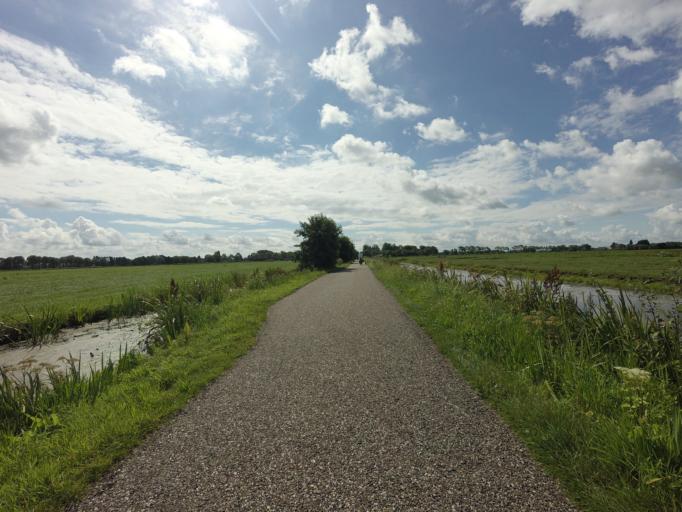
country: NL
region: South Holland
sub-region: Molenwaard
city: Liesveld
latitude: 51.9415
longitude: 4.8114
